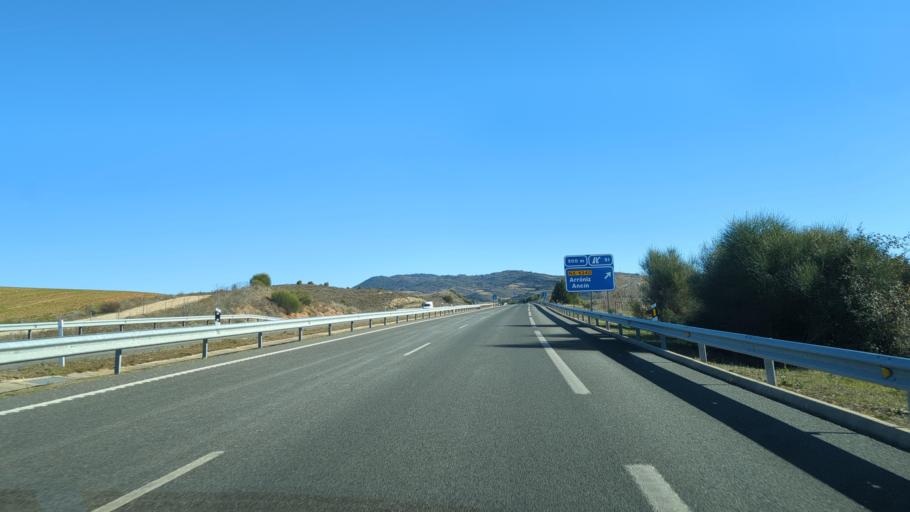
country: ES
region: Navarre
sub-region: Provincia de Navarra
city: Olejua
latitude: 42.5964
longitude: -2.1318
